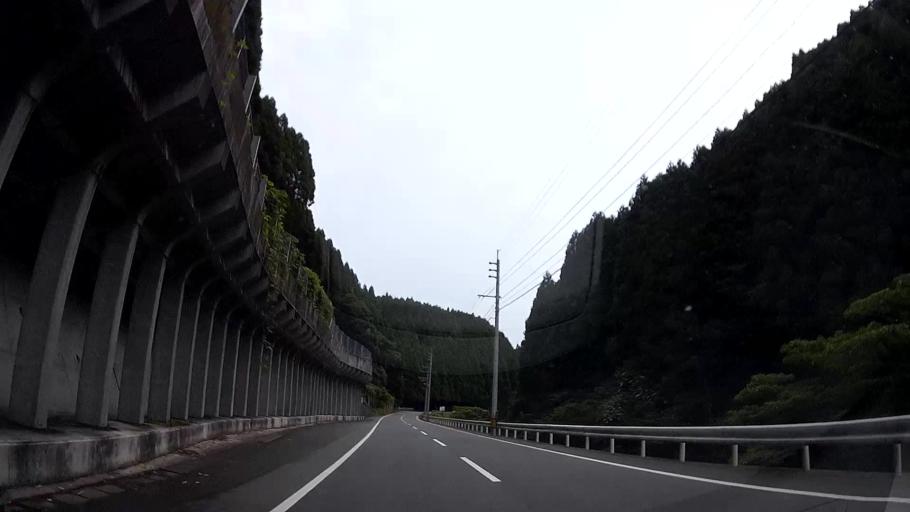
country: JP
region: Kumamoto
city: Kikuchi
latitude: 33.0365
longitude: 130.8909
